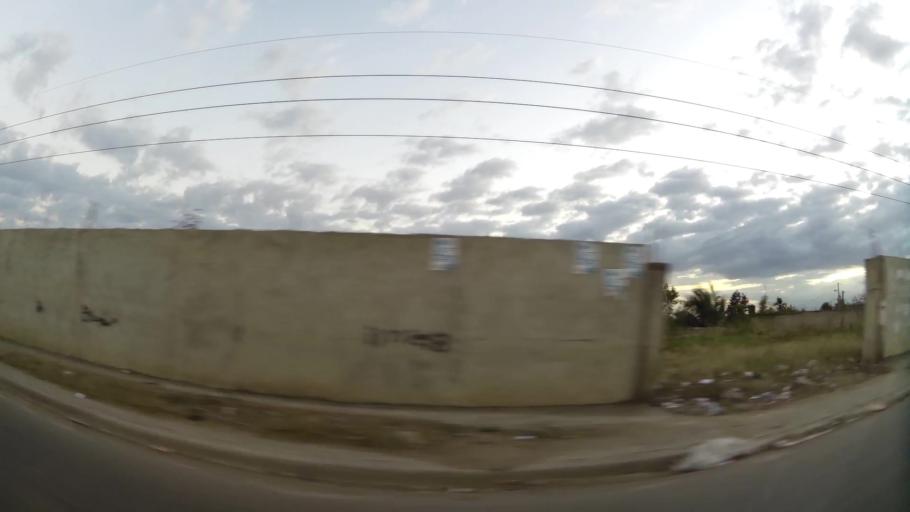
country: DO
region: Nacional
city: La Agustina
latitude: 18.5544
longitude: -69.9471
